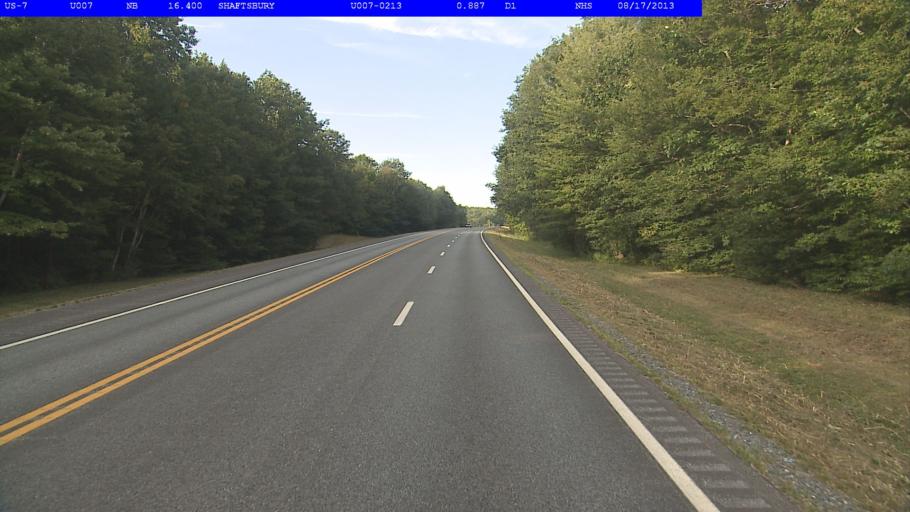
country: US
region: Vermont
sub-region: Bennington County
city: North Bennington
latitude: 42.9434
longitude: -73.1801
